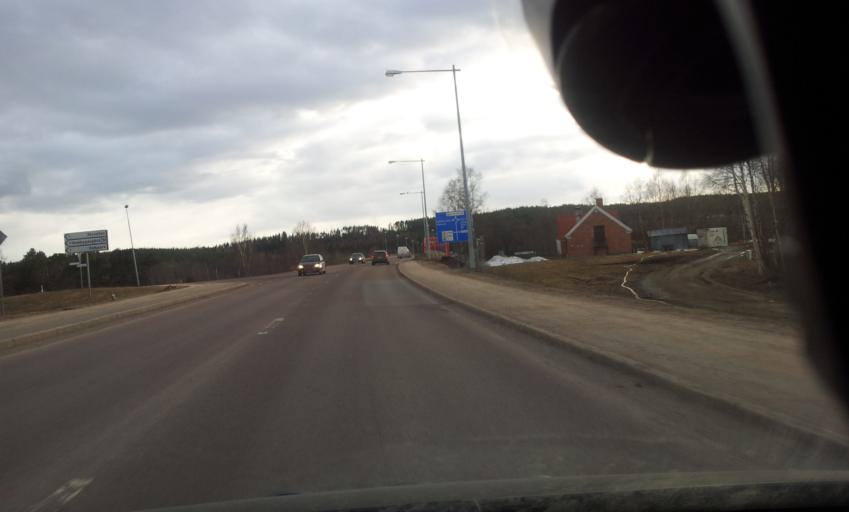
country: SE
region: Gaevleborg
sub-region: Ljusdals Kommun
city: Ljusdal
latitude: 61.8261
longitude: 16.0707
